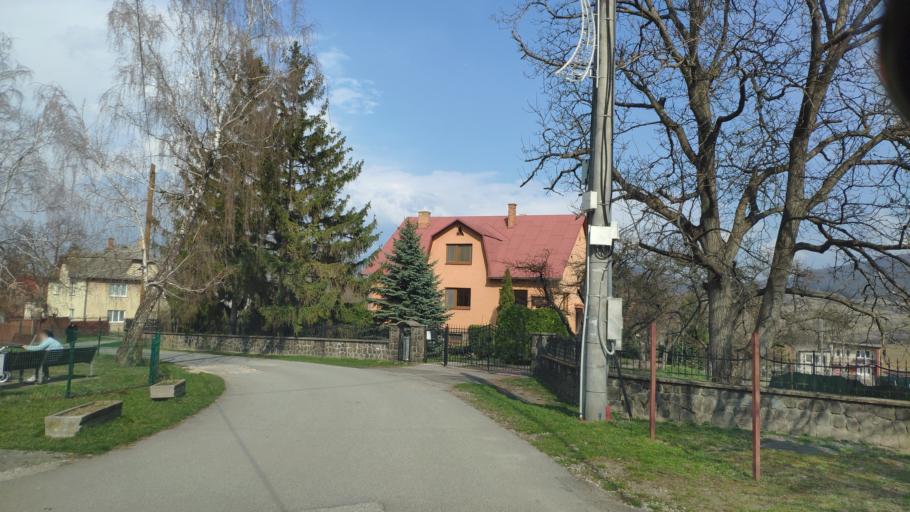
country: SK
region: Kosicky
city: Kosice
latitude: 48.6231
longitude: 21.3687
